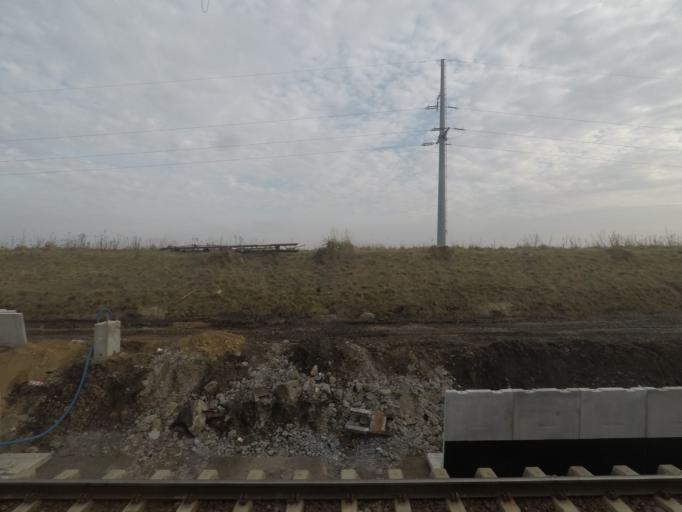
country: PL
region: Subcarpathian Voivodeship
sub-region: Powiat jaroslawski
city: Sosnica
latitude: 49.8612
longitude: 22.8564
